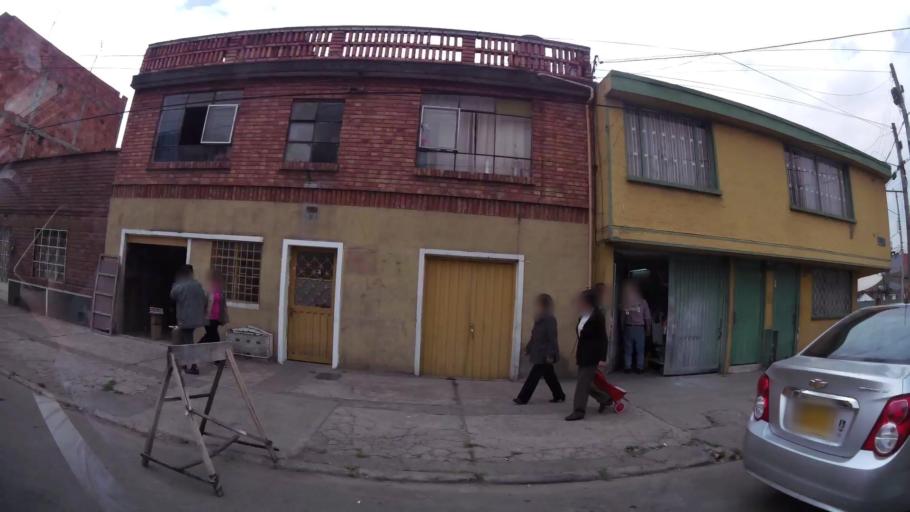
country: CO
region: Bogota D.C.
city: Barrio San Luis
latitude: 4.6840
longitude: -74.0672
